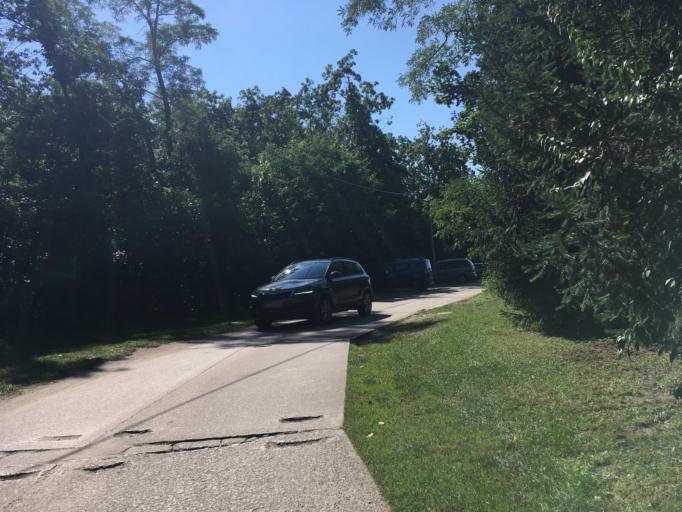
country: DE
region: Brandenburg
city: Gross Koris
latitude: 52.1860
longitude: 13.7103
